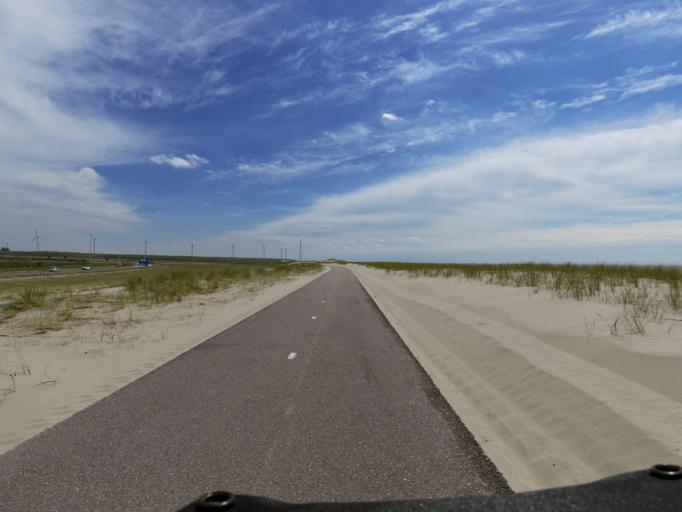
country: NL
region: South Holland
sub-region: Gemeente Goeree-Overflakkee
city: Goedereede
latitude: 51.9388
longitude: 3.9742
